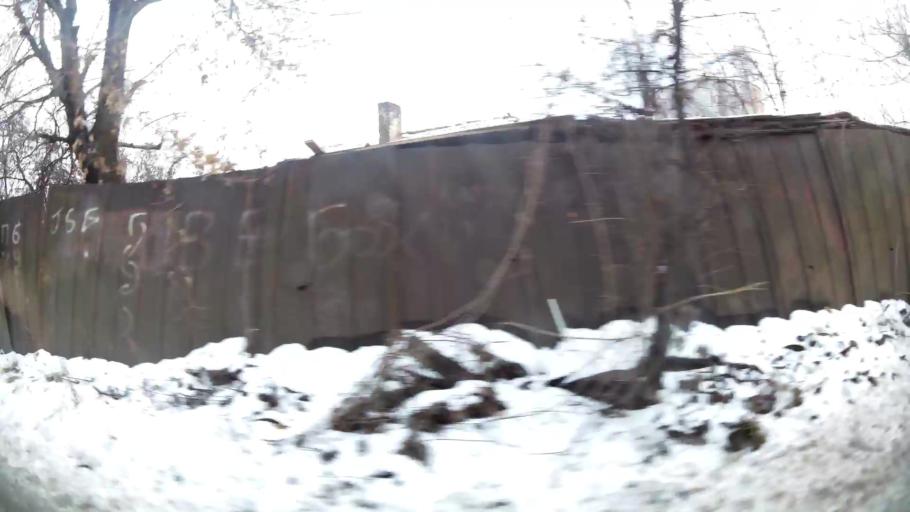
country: BG
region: Sofia-Capital
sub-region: Stolichna Obshtina
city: Sofia
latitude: 42.6964
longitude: 23.3690
